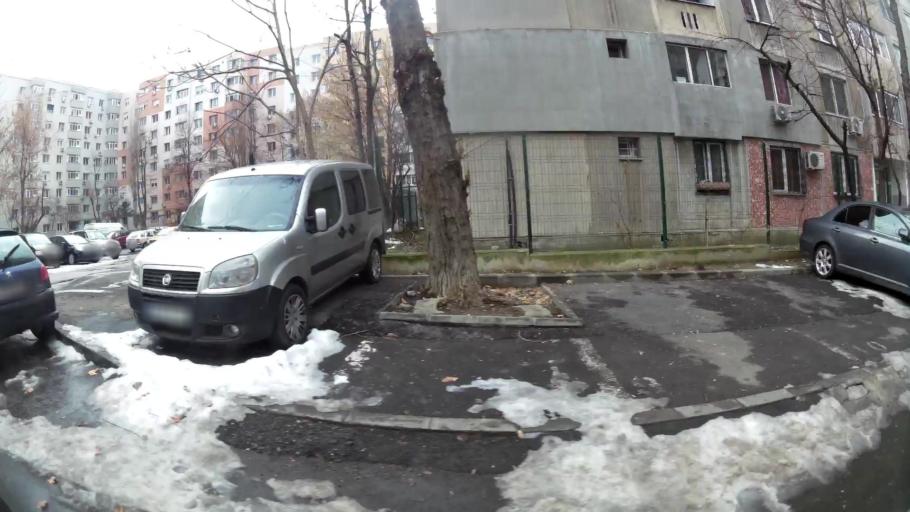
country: RO
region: Ilfov
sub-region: Comuna Popesti-Leordeni
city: Popesti-Leordeni
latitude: 44.4130
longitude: 26.1479
